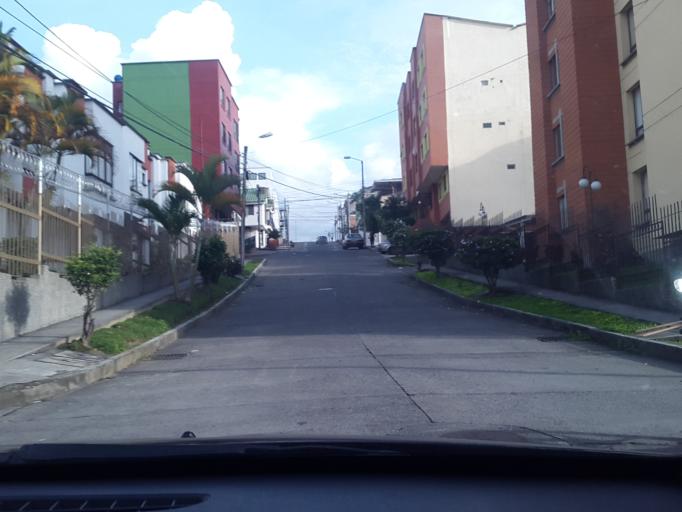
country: CO
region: Quindio
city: Armenia
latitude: 4.5401
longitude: -75.6680
